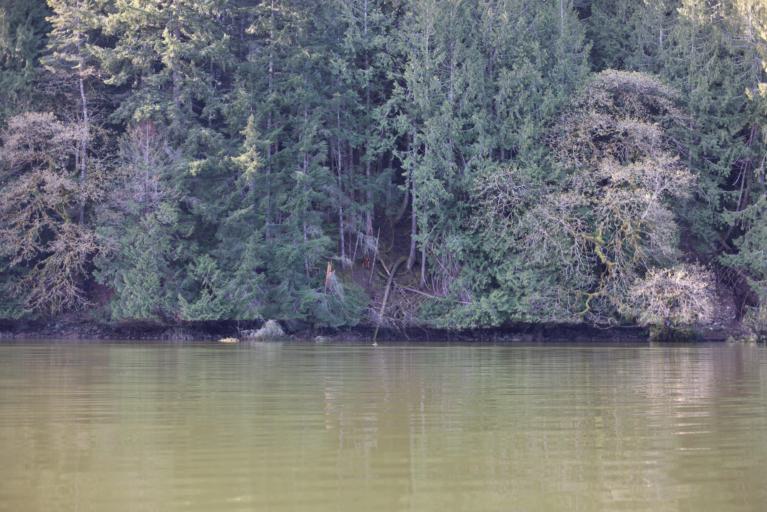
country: CA
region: British Columbia
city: Langford
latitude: 48.5585
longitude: -123.4714
